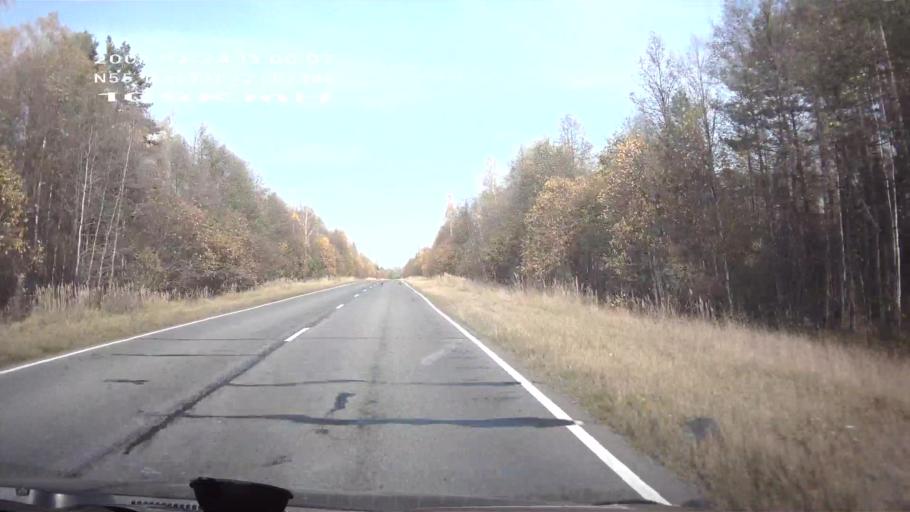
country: RU
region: Chuvashia
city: Buinsk
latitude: 55.1838
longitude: 47.0674
